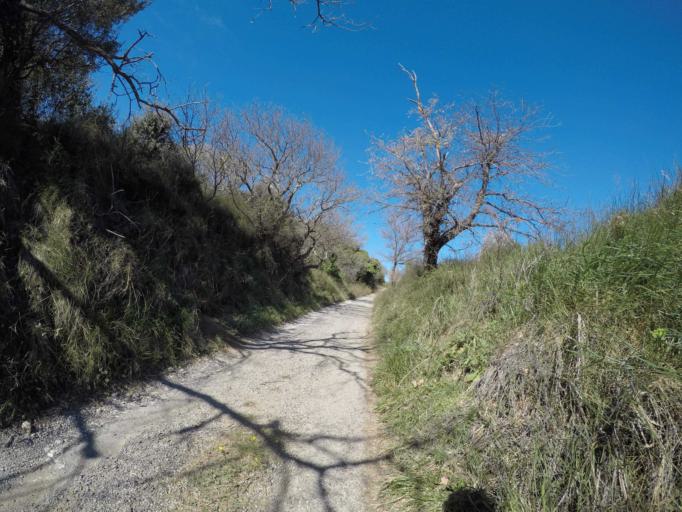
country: FR
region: Languedoc-Roussillon
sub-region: Departement des Pyrenees-Orientales
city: Millas
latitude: 42.7049
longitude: 2.6756
